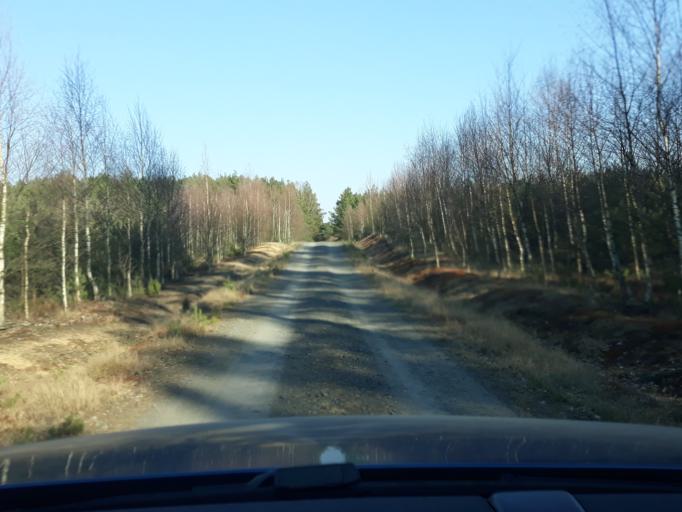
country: PL
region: Pomeranian Voivodeship
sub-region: Powiat bytowski
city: Lipnica
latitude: 53.9136
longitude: 17.4876
